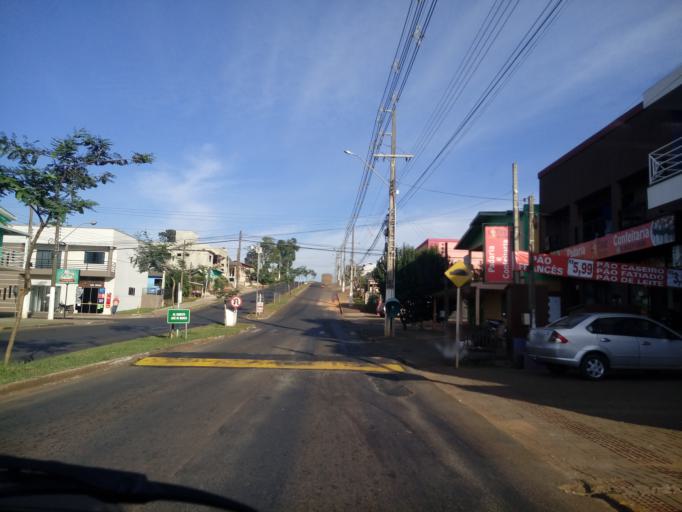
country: BR
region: Santa Catarina
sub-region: Chapeco
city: Chapeco
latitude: -27.0899
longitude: -52.6736
